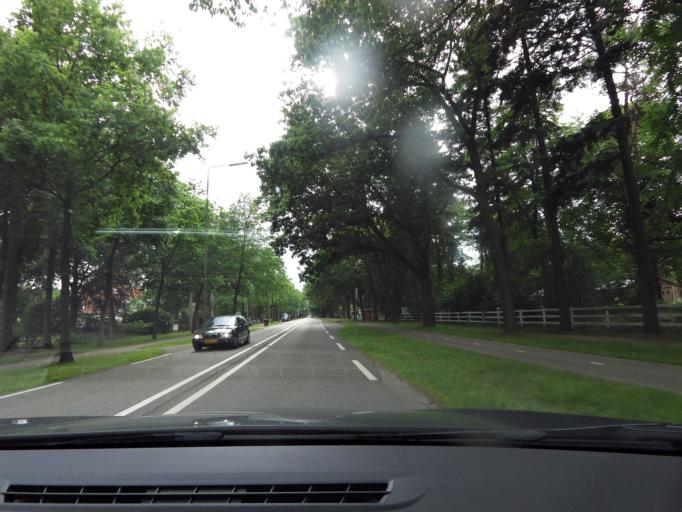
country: NL
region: Utrecht
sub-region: Gemeente Soest
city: Soest
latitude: 52.1316
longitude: 5.3244
